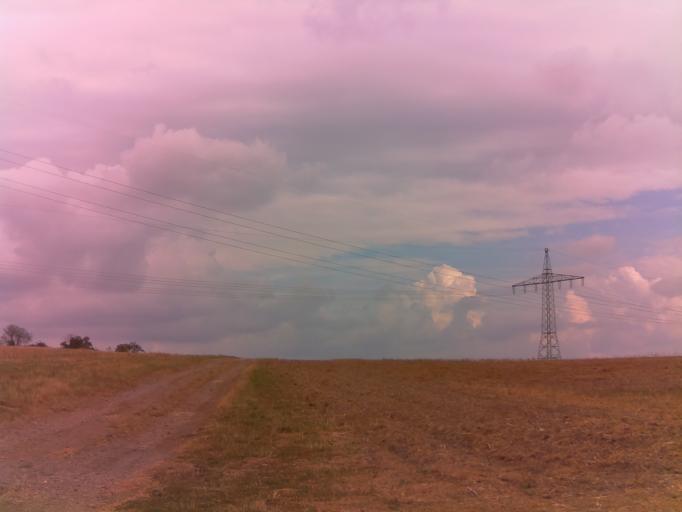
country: DE
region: Thuringia
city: Gosswitz
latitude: 50.6294
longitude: 11.5000
